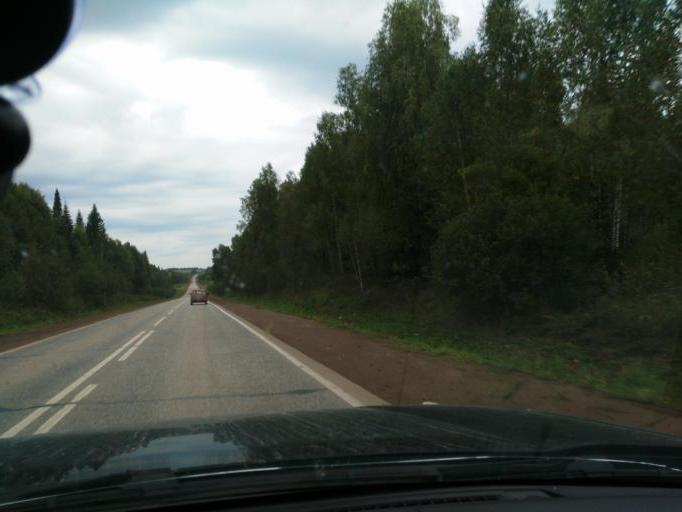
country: RU
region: Perm
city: Chernushka
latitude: 56.8020
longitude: 56.0672
